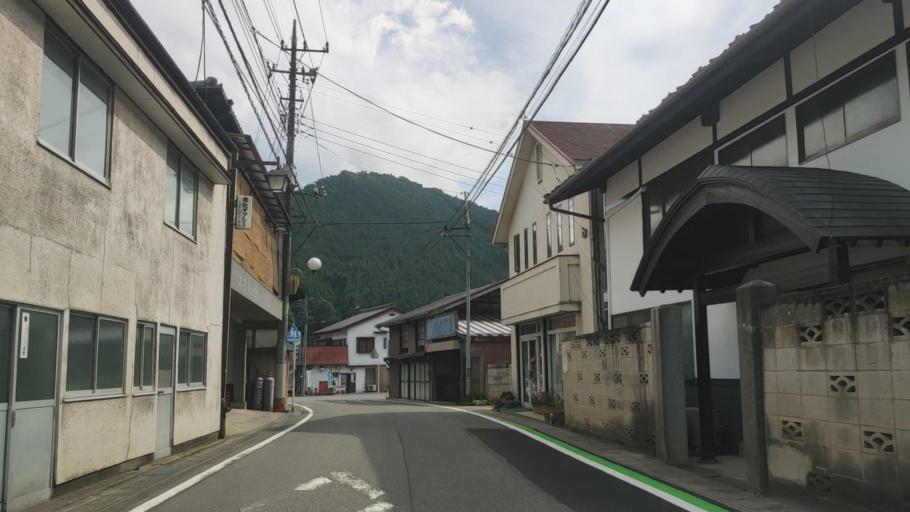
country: JP
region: Gunma
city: Tomioka
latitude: 36.1687
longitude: 138.7283
